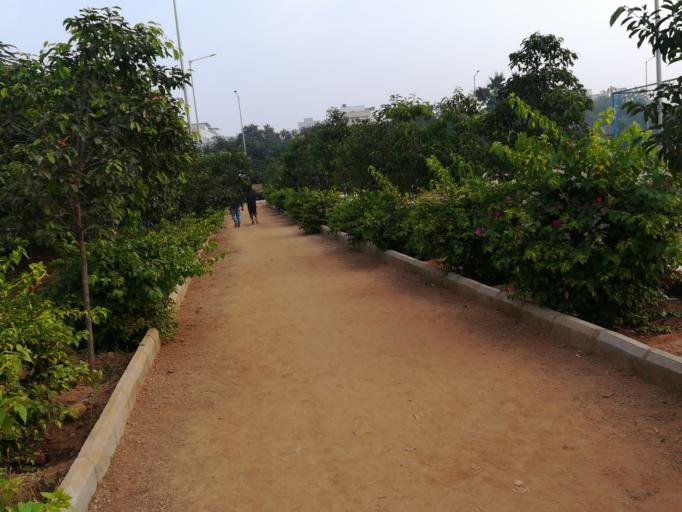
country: IN
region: Telangana
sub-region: Rangareddi
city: Kukatpalli
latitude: 17.4855
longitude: 78.3995
